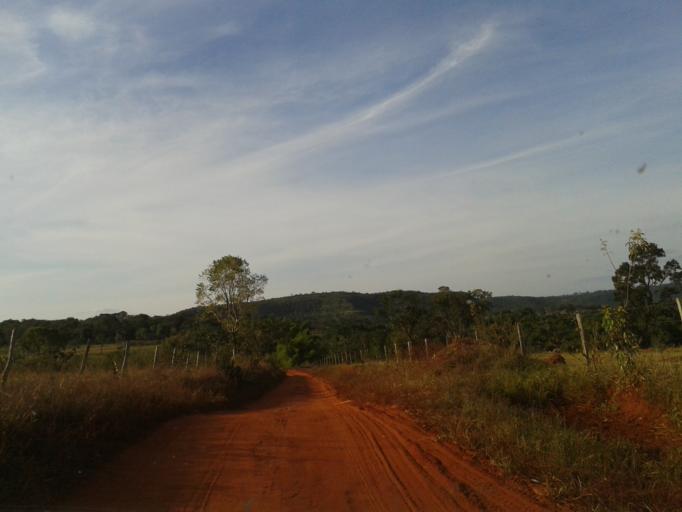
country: BR
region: Minas Gerais
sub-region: Campina Verde
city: Campina Verde
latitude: -19.5100
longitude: -49.6081
